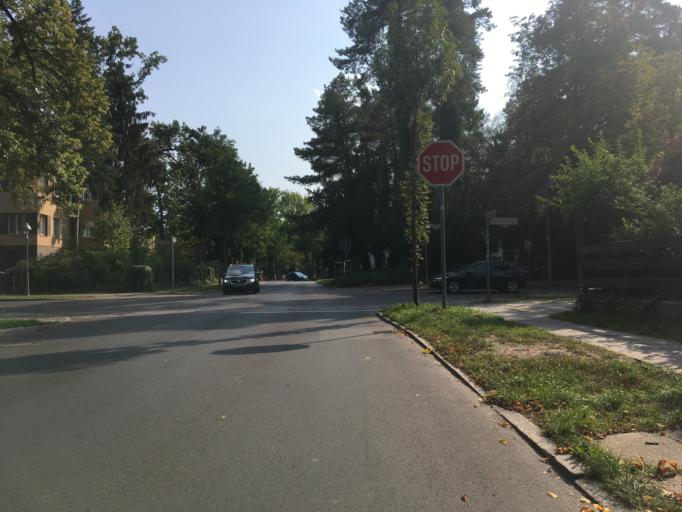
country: DE
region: Berlin
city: Frohnau
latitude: 52.6304
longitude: 13.2804
